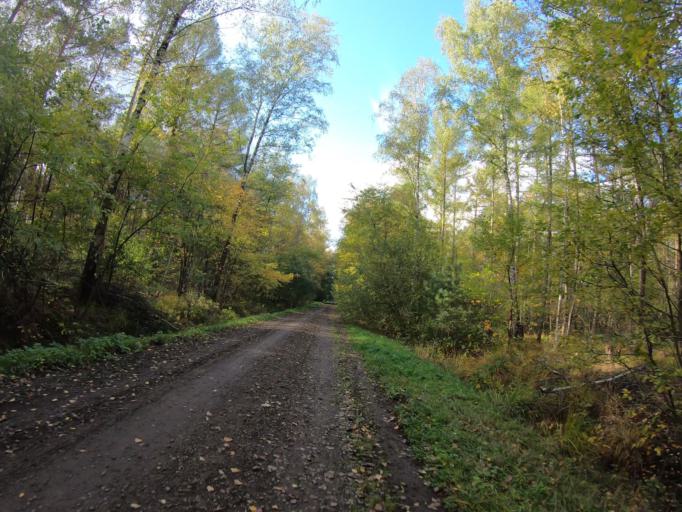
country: DE
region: Lower Saxony
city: Gifhorn
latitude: 52.5073
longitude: 10.5717
